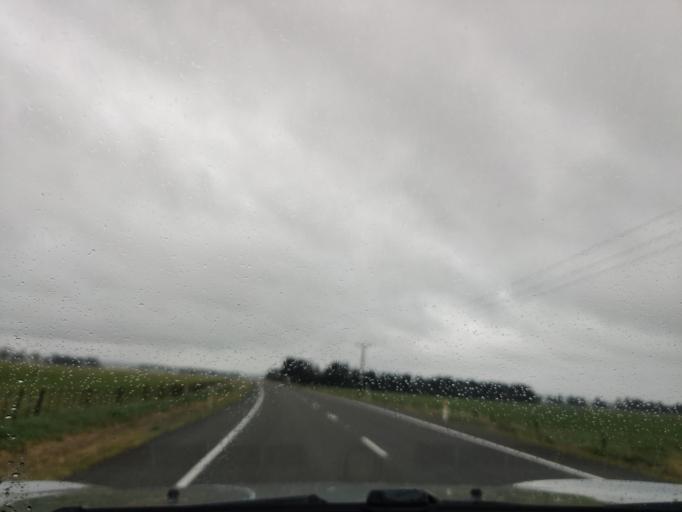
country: NZ
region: Hawke's Bay
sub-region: Hastings District
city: Hastings
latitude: -40.0153
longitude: 176.3601
